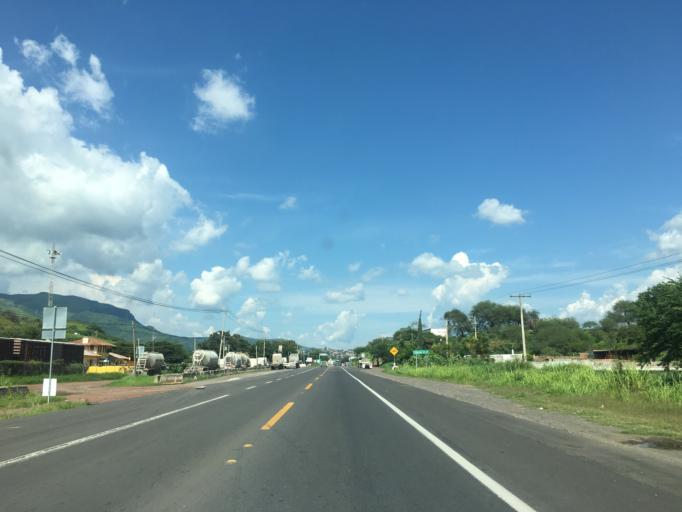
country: MX
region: Nayarit
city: Ixtlan del Rio
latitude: 21.0372
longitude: -104.3913
